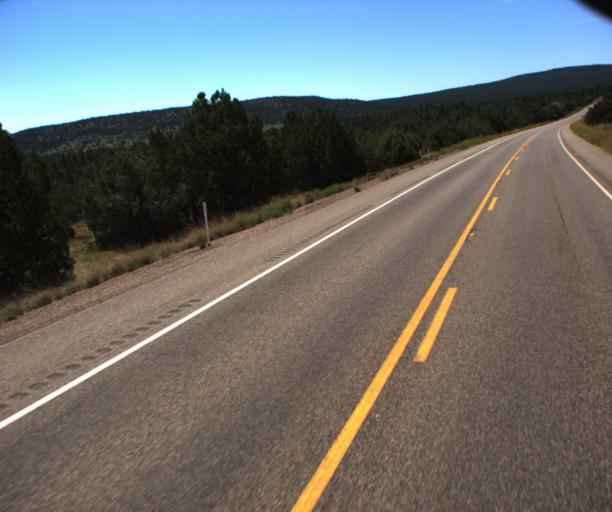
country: US
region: Arizona
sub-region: Navajo County
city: Cibecue
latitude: 33.7117
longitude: -110.5355
